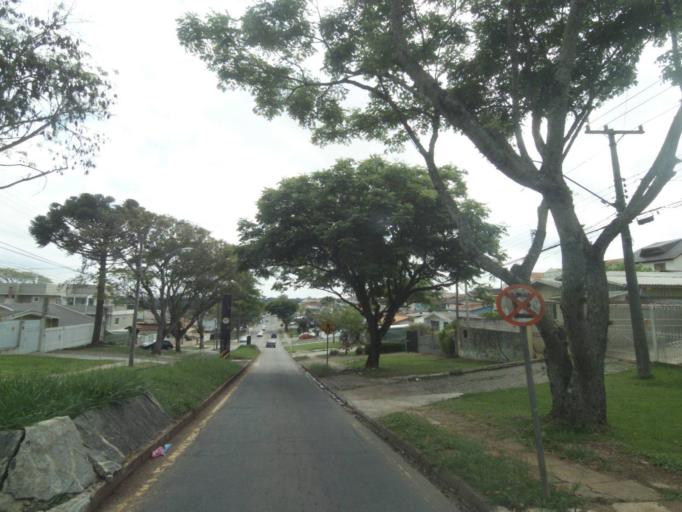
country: BR
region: Parana
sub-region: Pinhais
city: Pinhais
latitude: -25.4145
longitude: -49.2122
